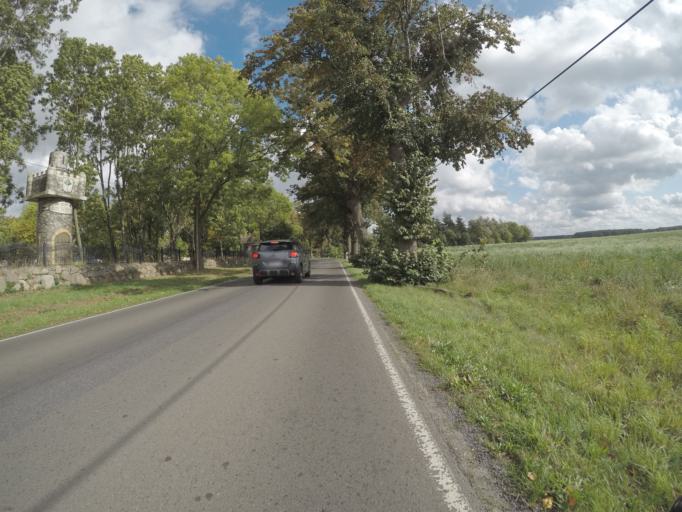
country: DE
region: Brandenburg
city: Altlandsberg
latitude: 52.5803
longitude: 13.7659
